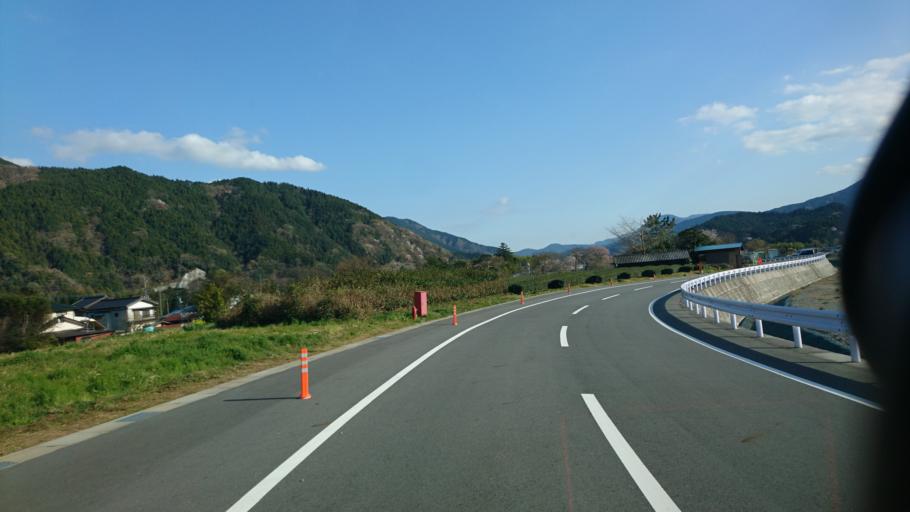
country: JP
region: Shizuoka
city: Fujinomiya
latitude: 35.3054
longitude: 138.4487
